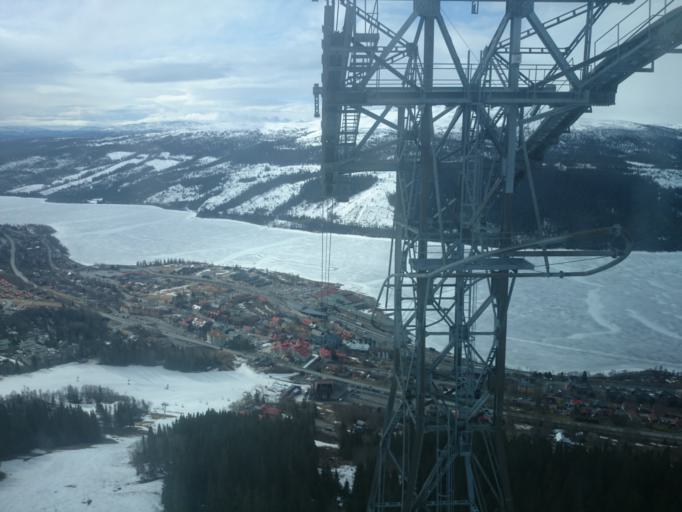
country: SE
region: Jaemtland
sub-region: Are Kommun
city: Are
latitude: 63.4078
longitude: 13.0770
